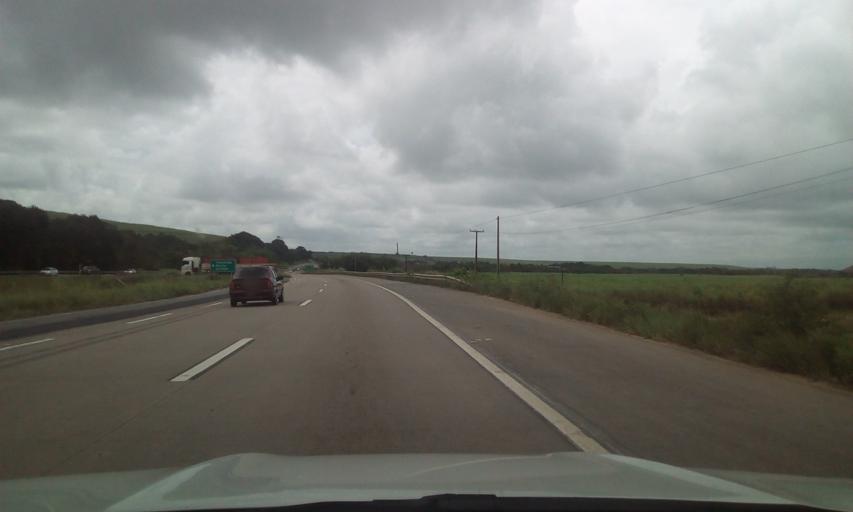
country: BR
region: Pernambuco
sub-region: Itapissuma
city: Itapissuma
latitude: -7.7609
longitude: -34.9354
